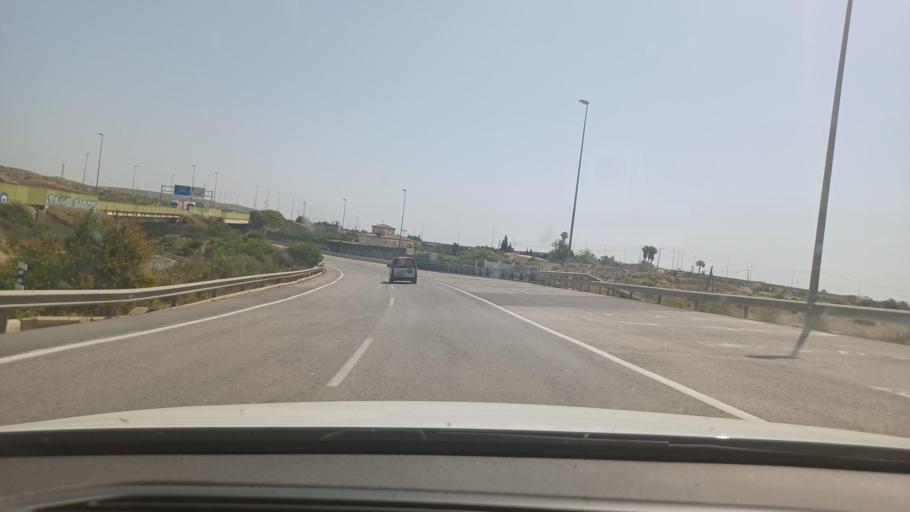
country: ES
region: Valencia
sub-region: Provincia de Alicante
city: Elche
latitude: 38.2973
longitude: -0.6750
